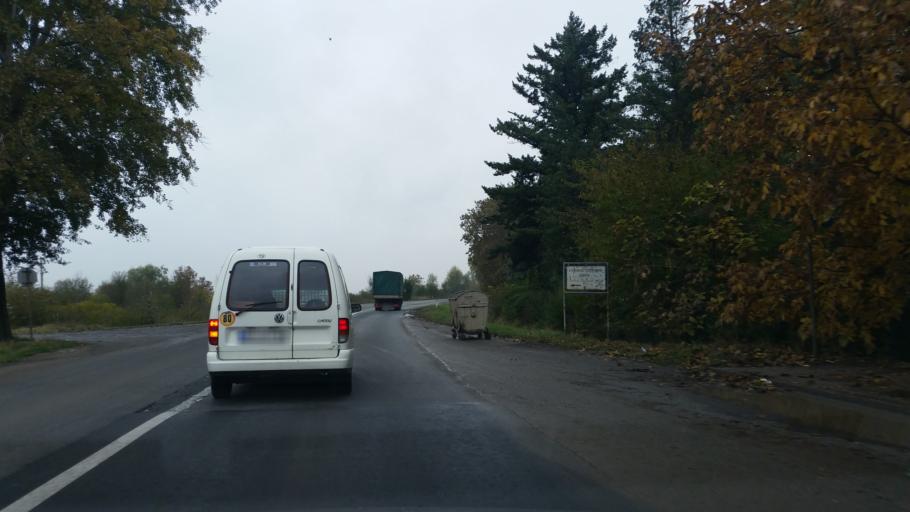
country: RS
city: Sefkerin
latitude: 44.9541
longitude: 20.4282
